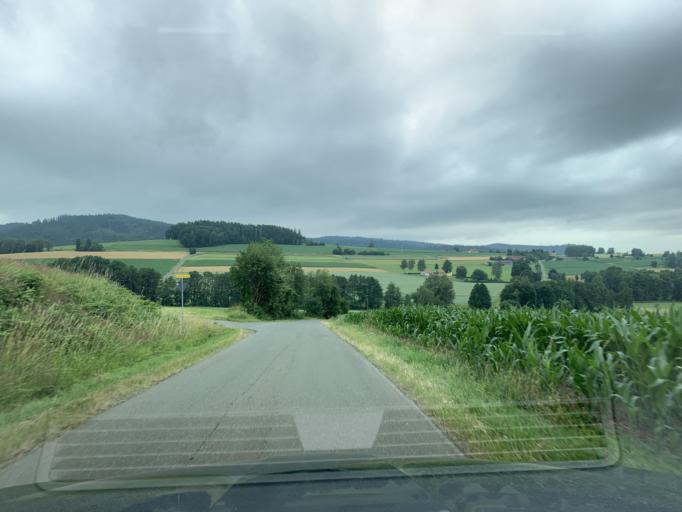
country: DE
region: Bavaria
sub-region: Upper Palatinate
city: Dieterskirchen
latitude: 49.4079
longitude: 12.4259
